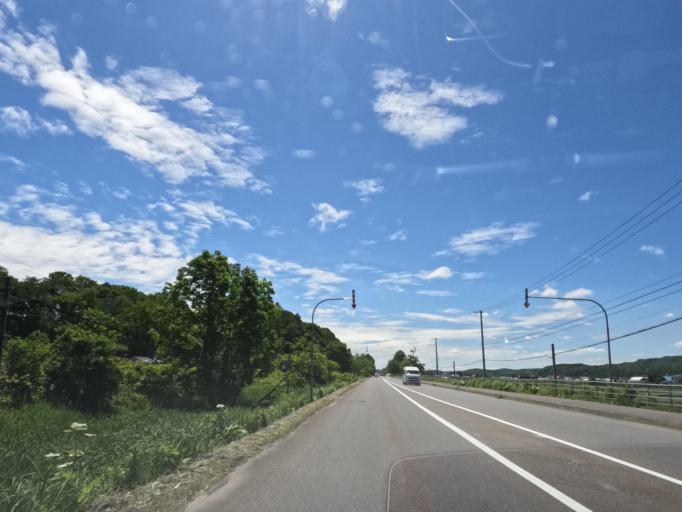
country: JP
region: Hokkaido
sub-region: Asahikawa-shi
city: Asahikawa
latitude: 43.7197
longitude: 142.3719
